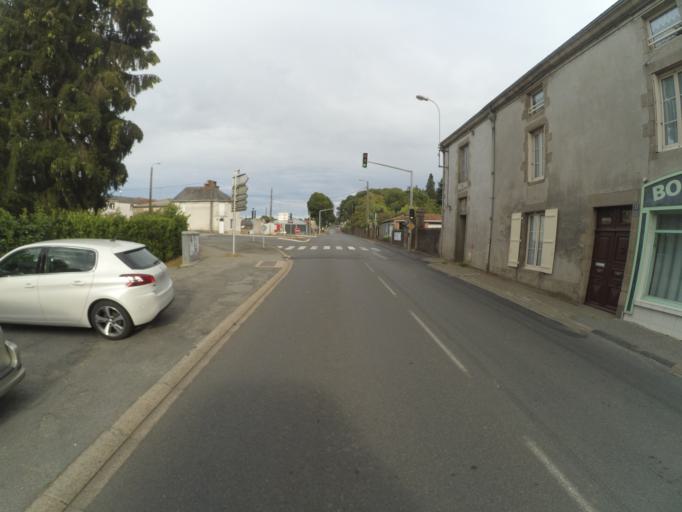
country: FR
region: Poitou-Charentes
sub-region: Departement des Deux-Sevres
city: Saint-Pierre-des-Echaubrognes
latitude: 46.9252
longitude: -0.7557
